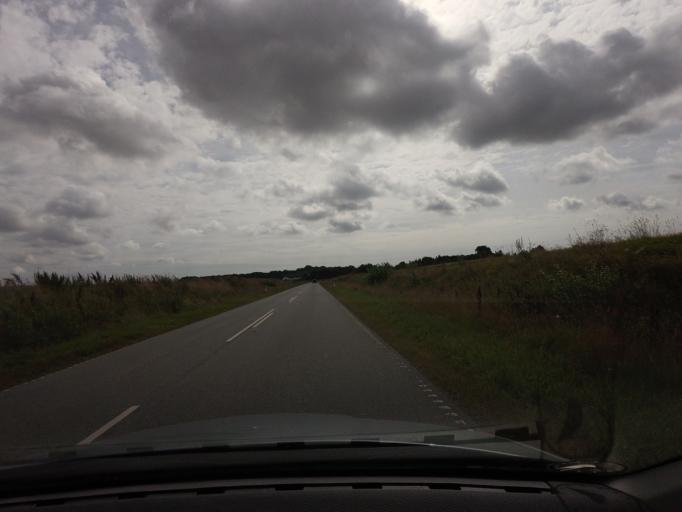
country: DK
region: North Denmark
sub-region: Bronderslev Kommune
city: Dronninglund
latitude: 57.2803
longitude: 10.3474
